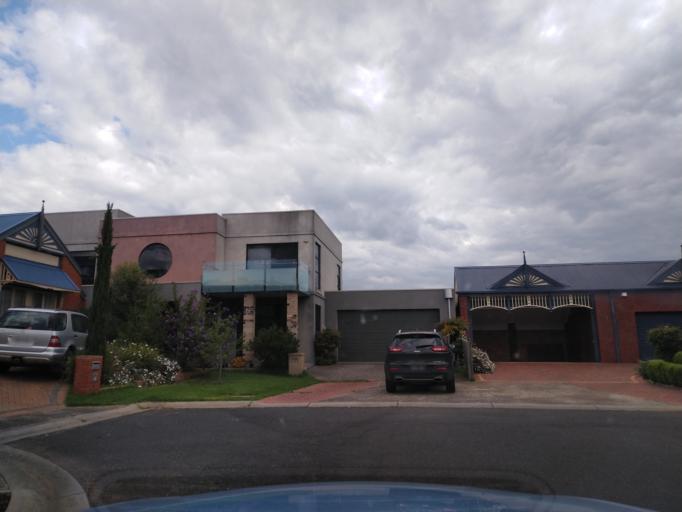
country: AU
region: Victoria
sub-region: Hobsons Bay
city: Williamstown North
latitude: -37.8537
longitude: 144.8720
